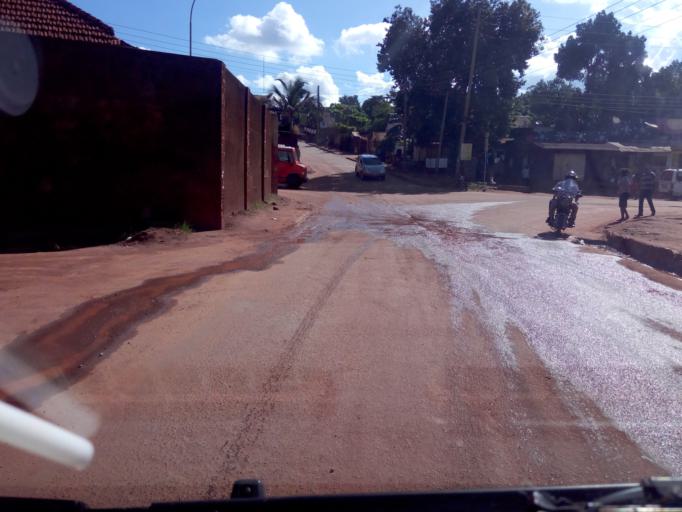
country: UG
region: Central Region
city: Kampala Central Division
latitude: 0.3184
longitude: 32.5669
